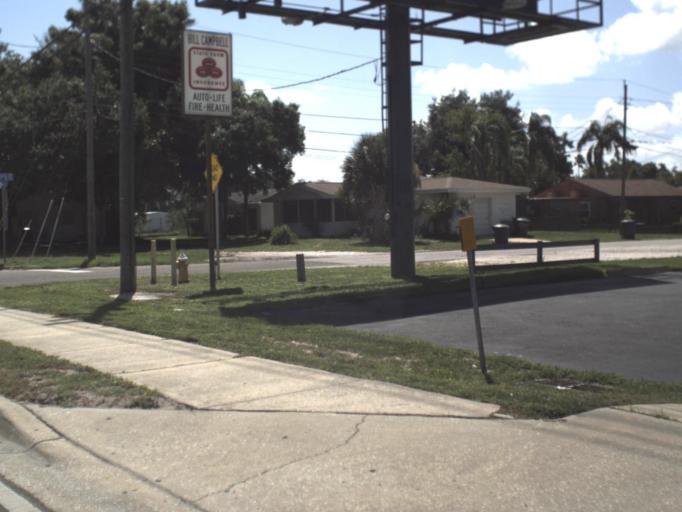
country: US
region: Florida
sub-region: Pinellas County
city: Largo
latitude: 27.9165
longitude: -82.7653
